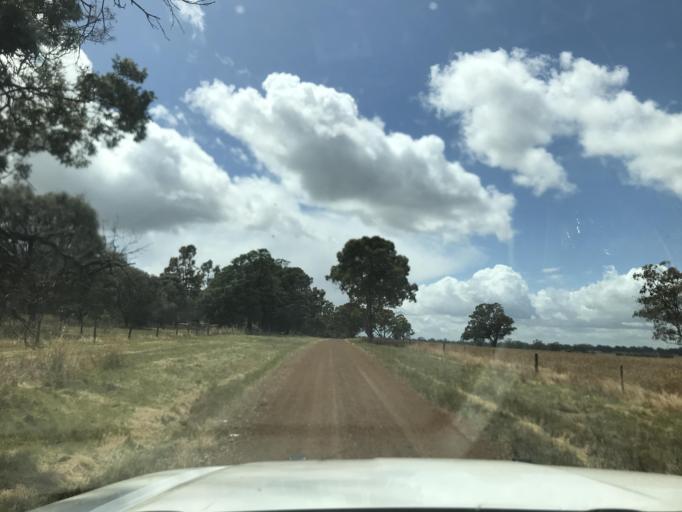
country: AU
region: South Australia
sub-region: Wattle Range
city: Penola
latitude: -37.1825
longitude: 141.4541
